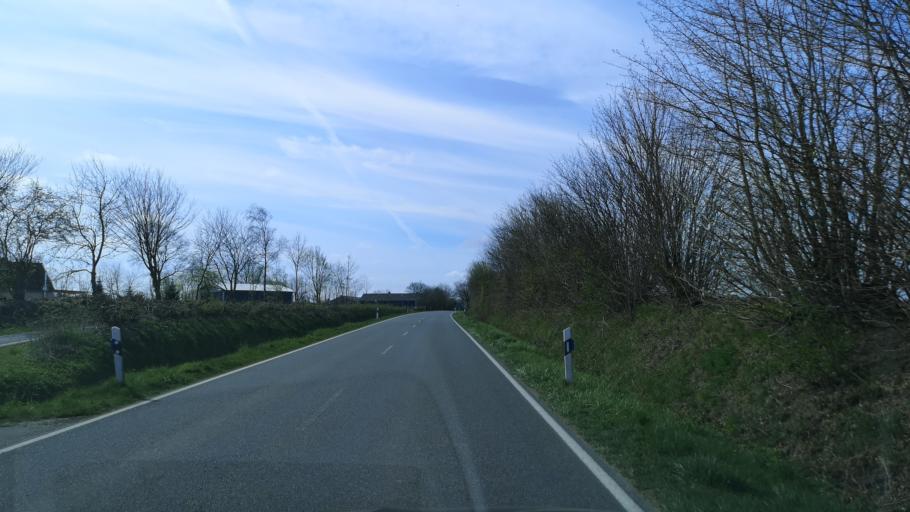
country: DE
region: Schleswig-Holstein
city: Osterrade
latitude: 54.1885
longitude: 9.3452
